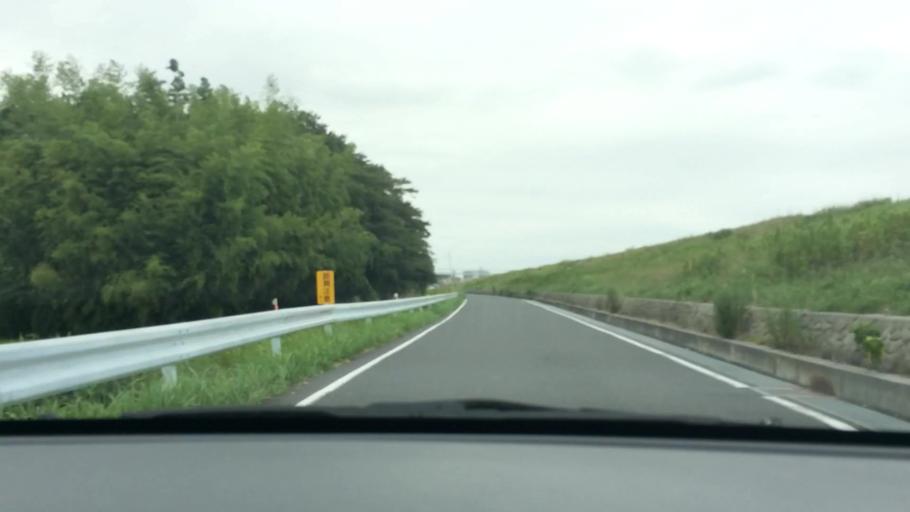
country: JP
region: Chiba
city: Nagareyama
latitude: 35.8318
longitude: 139.8860
